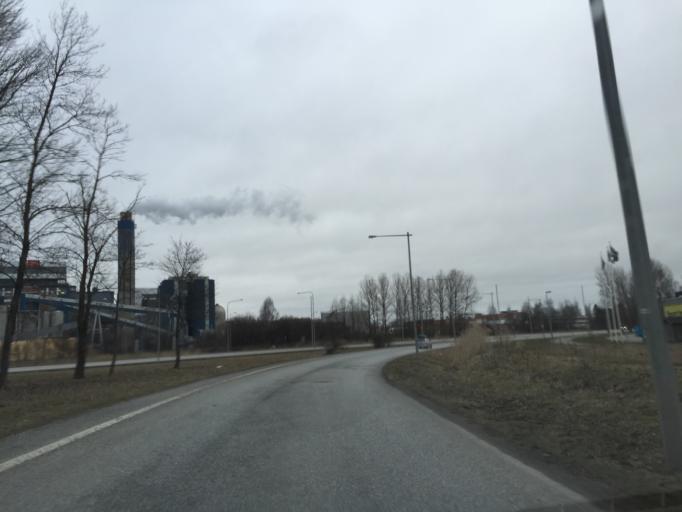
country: SE
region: OErebro
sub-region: Orebro Kommun
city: Orebro
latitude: 59.2620
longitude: 15.1776
